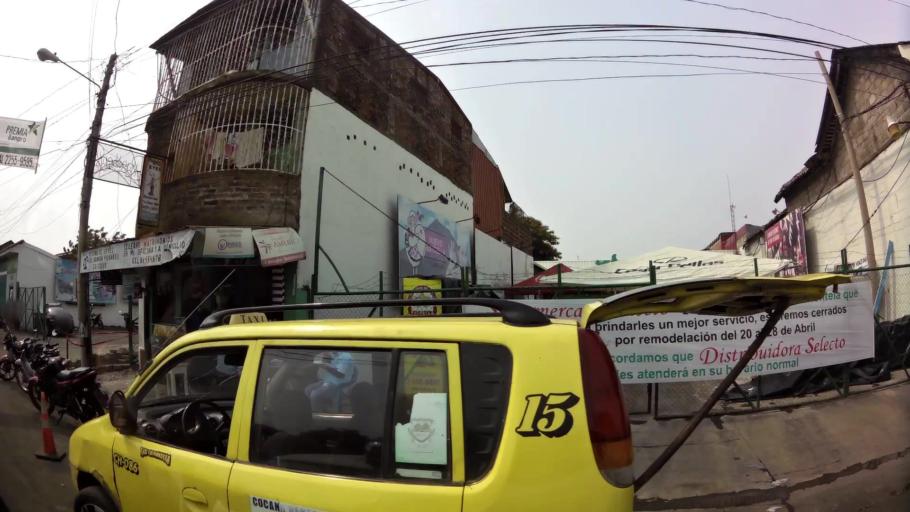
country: NI
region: Chinandega
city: Chinandega
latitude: 12.6295
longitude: -87.1307
